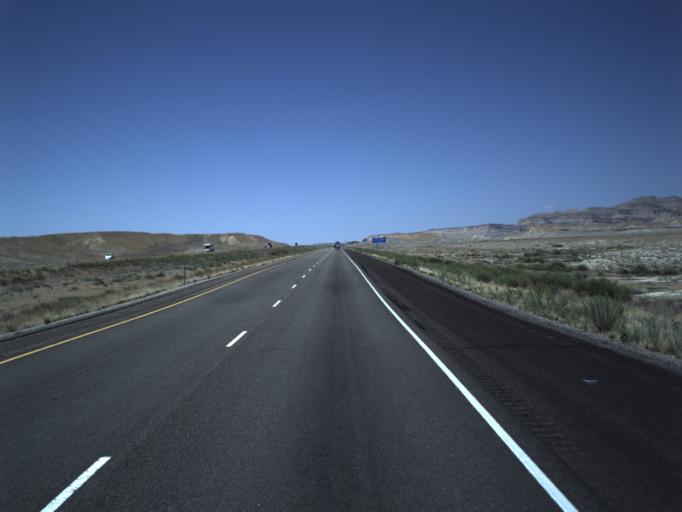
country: US
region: Utah
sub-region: Grand County
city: Moab
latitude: 38.9468
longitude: -109.6574
